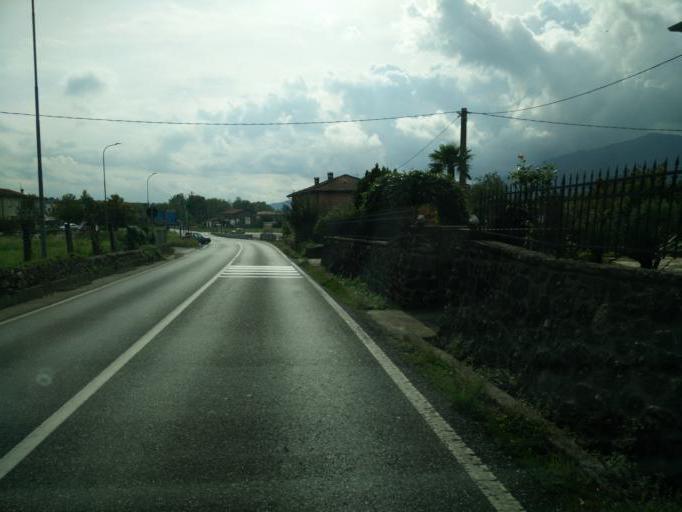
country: IT
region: Tuscany
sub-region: Provincia di Massa-Carrara
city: Filattiera
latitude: 44.3503
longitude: 9.9069
